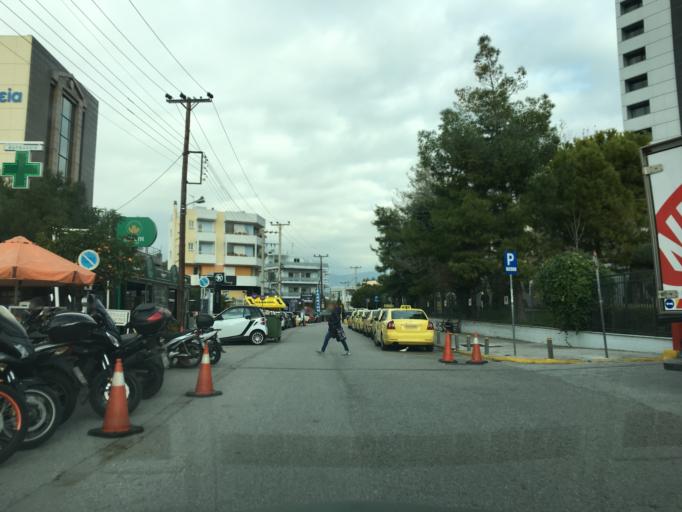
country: GR
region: Attica
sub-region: Nomarchia Athinas
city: Filothei
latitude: 38.0278
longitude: 23.7894
